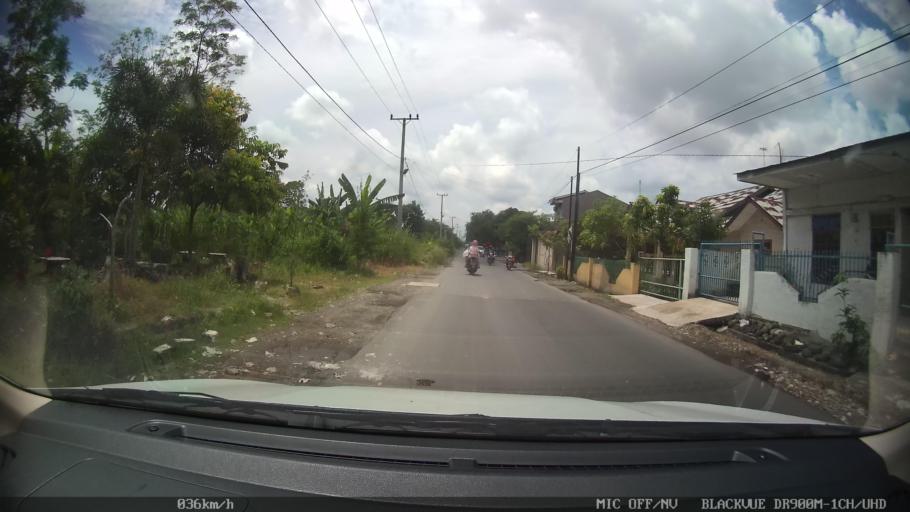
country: ID
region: North Sumatra
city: Medan
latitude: 3.6047
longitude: 98.7290
